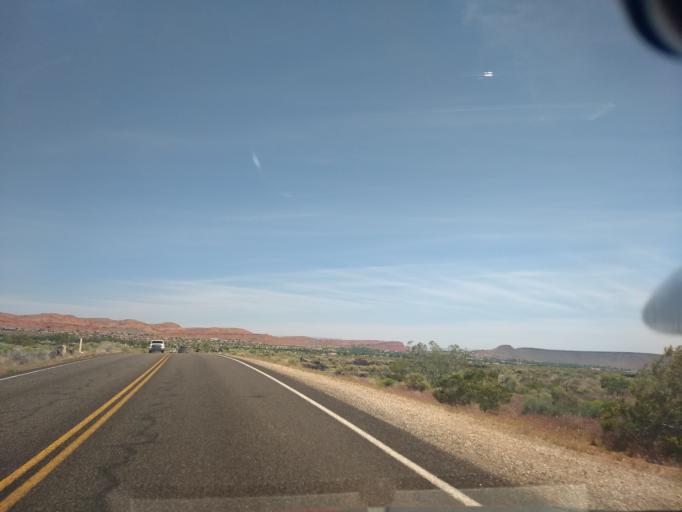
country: US
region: Utah
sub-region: Washington County
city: Santa Clara
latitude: 37.1441
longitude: -113.6496
